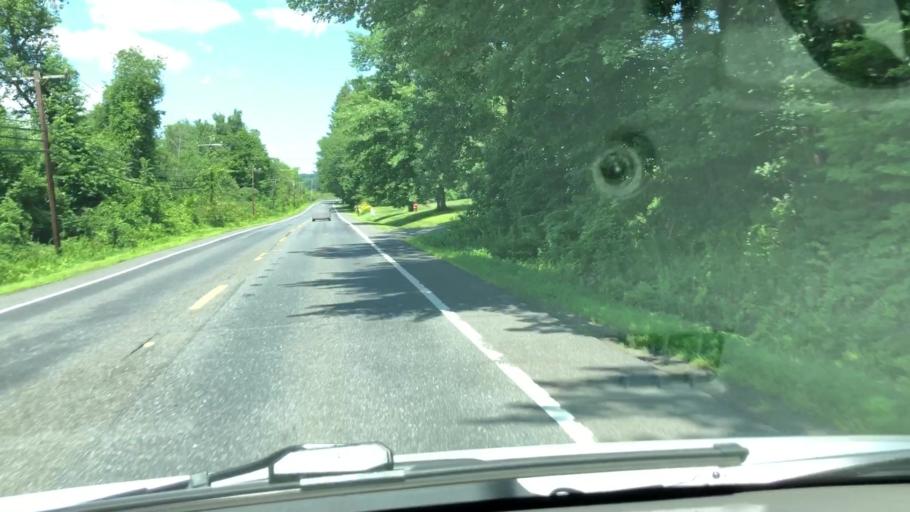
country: US
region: Massachusetts
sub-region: Franklin County
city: Greenfield
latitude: 42.5484
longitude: -72.6007
